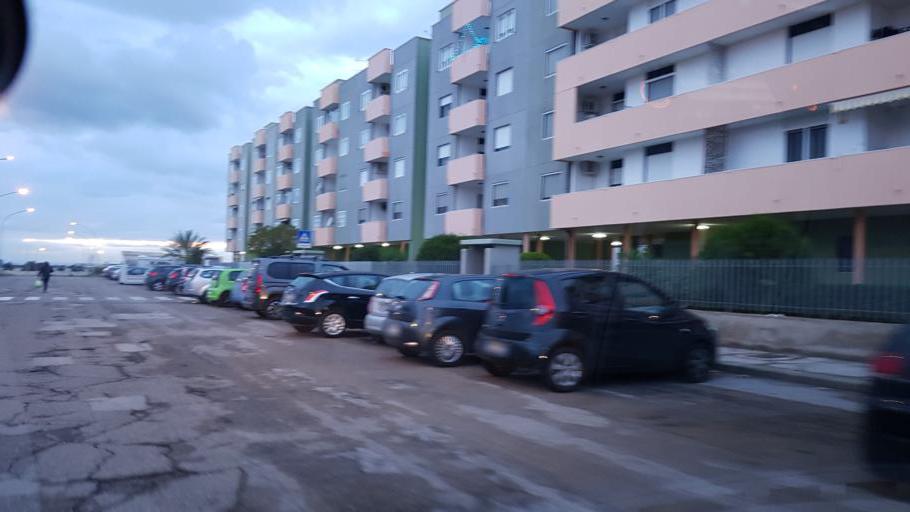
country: IT
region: Apulia
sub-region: Provincia di Taranto
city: Paolo VI
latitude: 40.5313
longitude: 17.2847
